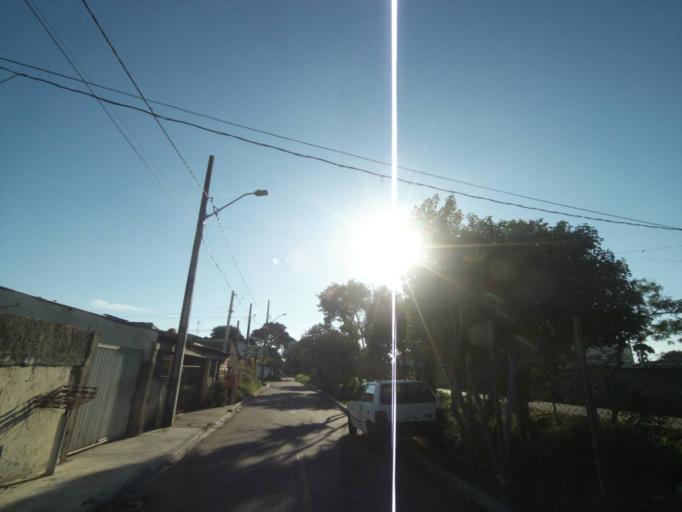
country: BR
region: Parana
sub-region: Pinhais
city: Pinhais
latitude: -25.4628
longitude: -49.2021
